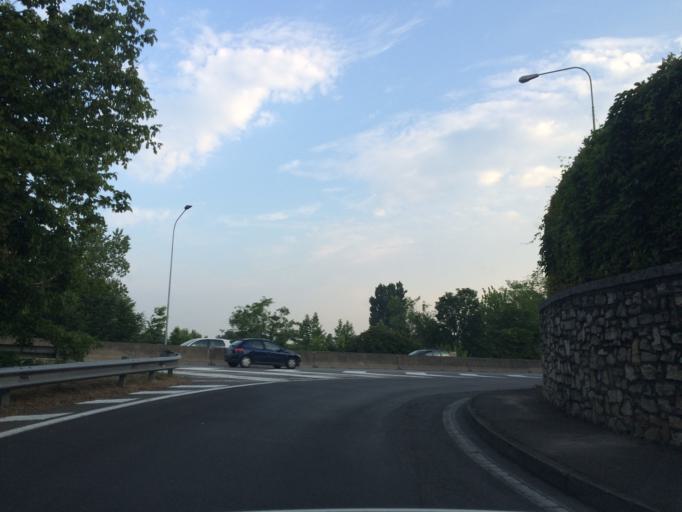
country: IT
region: Lombardy
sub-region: Provincia di Brescia
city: Castel Mella
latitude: 45.4943
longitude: 10.1599
